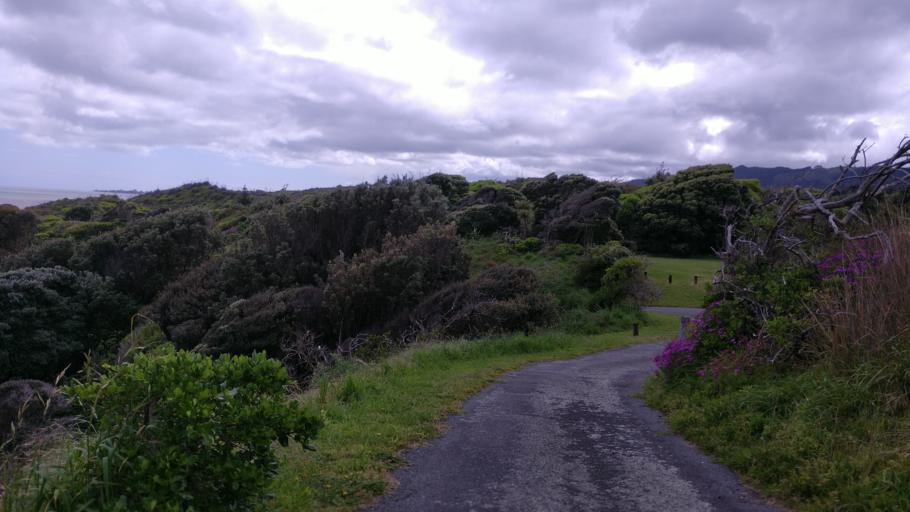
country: NZ
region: Wellington
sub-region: Kapiti Coast District
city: Paraparaumu
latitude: -40.9718
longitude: 174.9620
